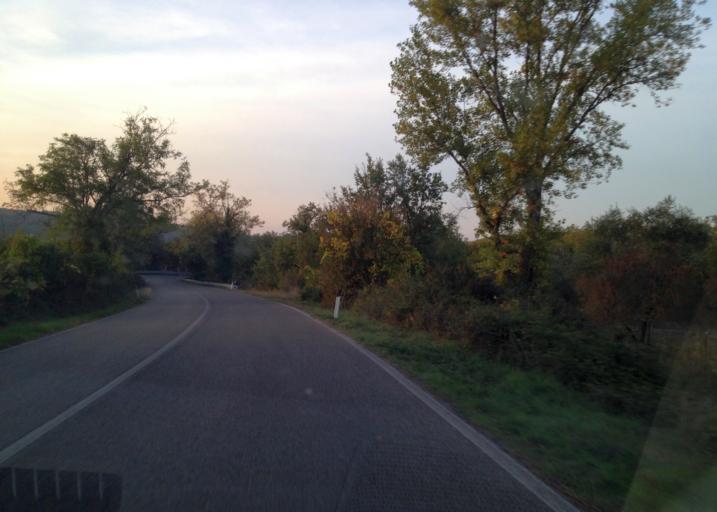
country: IT
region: Tuscany
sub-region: Provincia di Siena
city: Castellina in Chianti
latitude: 43.4970
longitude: 11.2992
